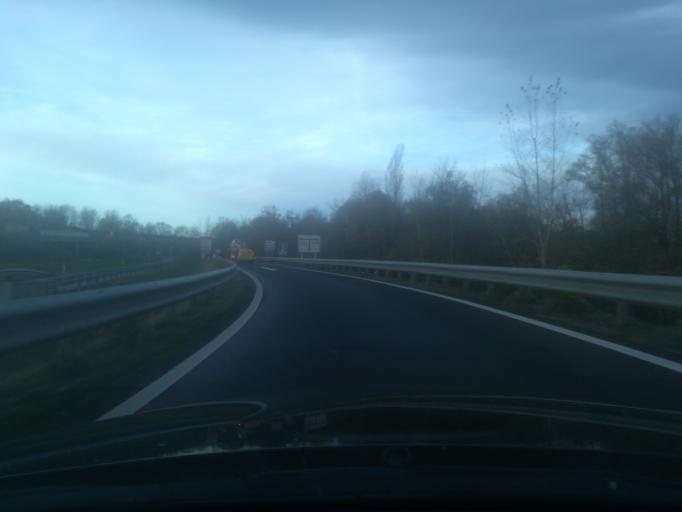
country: AT
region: Upper Austria
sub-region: Wels-Land
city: Marchtrenk
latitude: 48.1755
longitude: 14.1237
